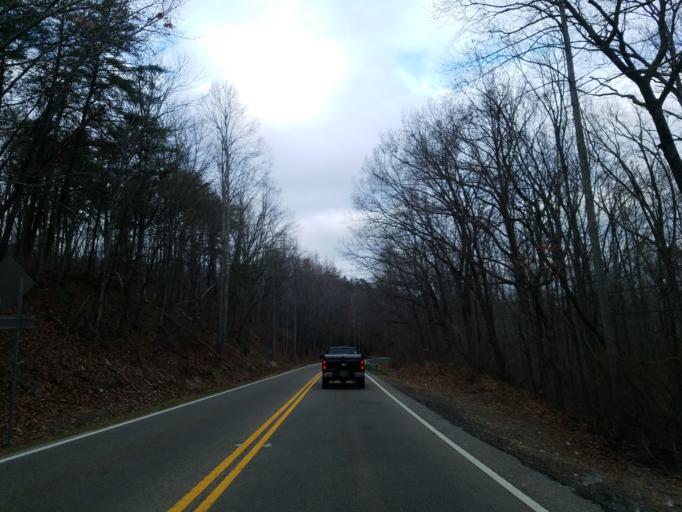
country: US
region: Georgia
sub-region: Cherokee County
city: Canton
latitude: 34.2884
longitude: -84.5206
